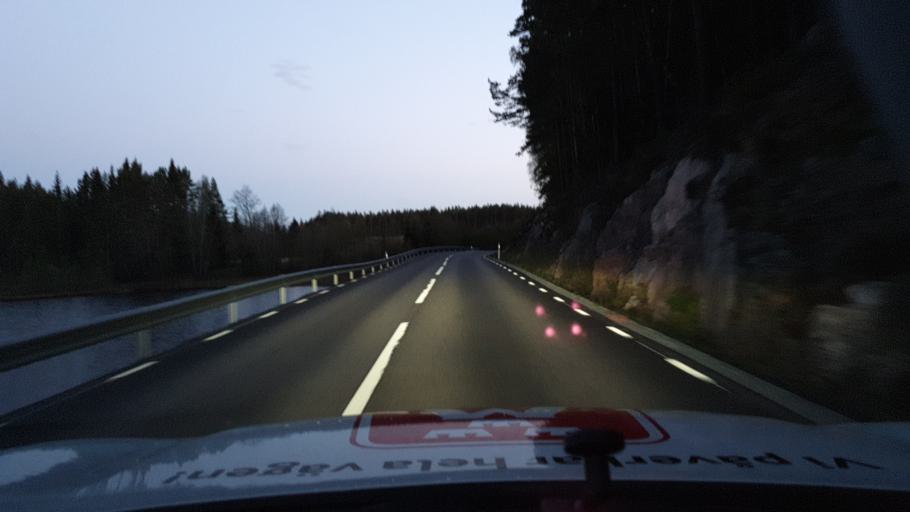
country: SE
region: OErebro
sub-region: Ljusnarsbergs Kommun
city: Kopparberg
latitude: 59.8030
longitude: 14.8306
